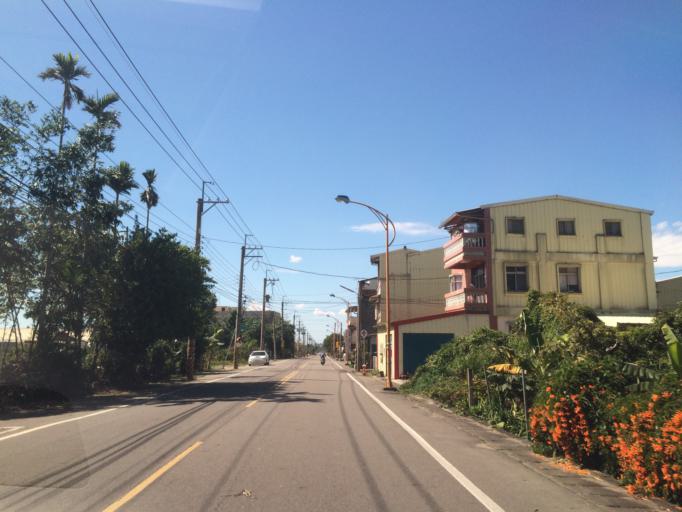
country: TW
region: Taiwan
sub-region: Yunlin
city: Douliu
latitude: 23.7032
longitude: 120.5939
